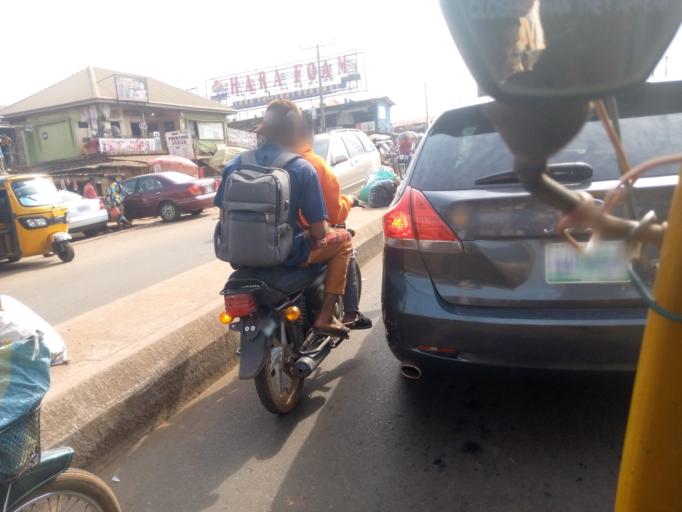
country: NG
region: Enugu
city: Nsukka
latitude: 6.8495
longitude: 7.3973
